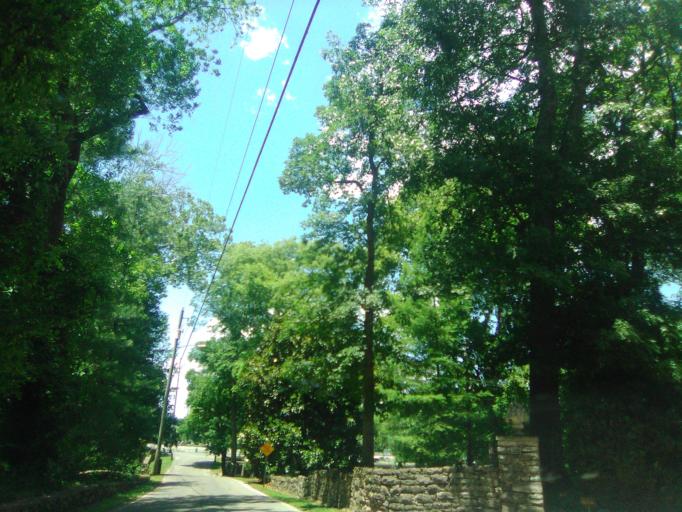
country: US
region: Tennessee
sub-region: Davidson County
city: Belle Meade
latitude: 36.1137
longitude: -86.8607
